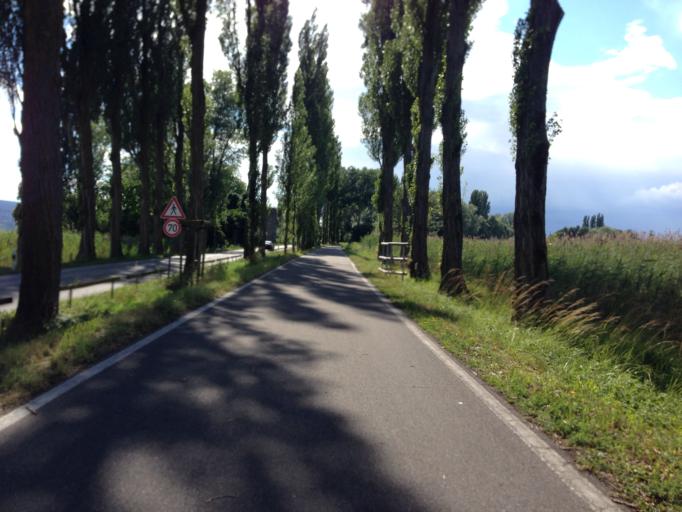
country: CH
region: Thurgau
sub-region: Kreuzlingen District
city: Ermatingen
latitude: 47.6867
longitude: 9.1024
